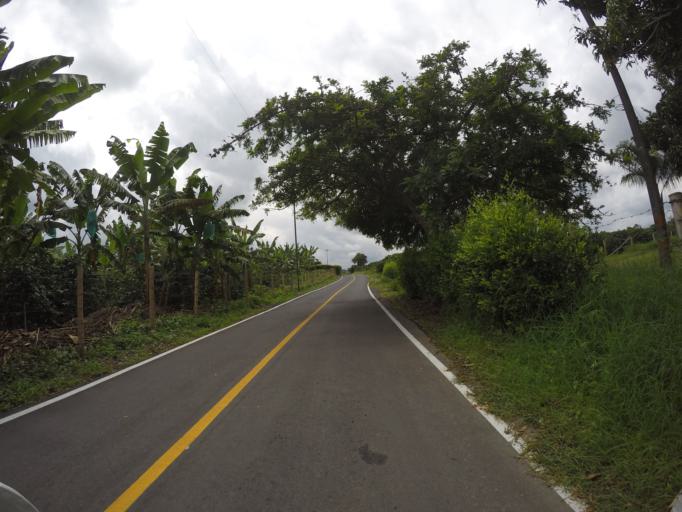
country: CO
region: Quindio
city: Quimbaya
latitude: 4.6140
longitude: -75.7497
